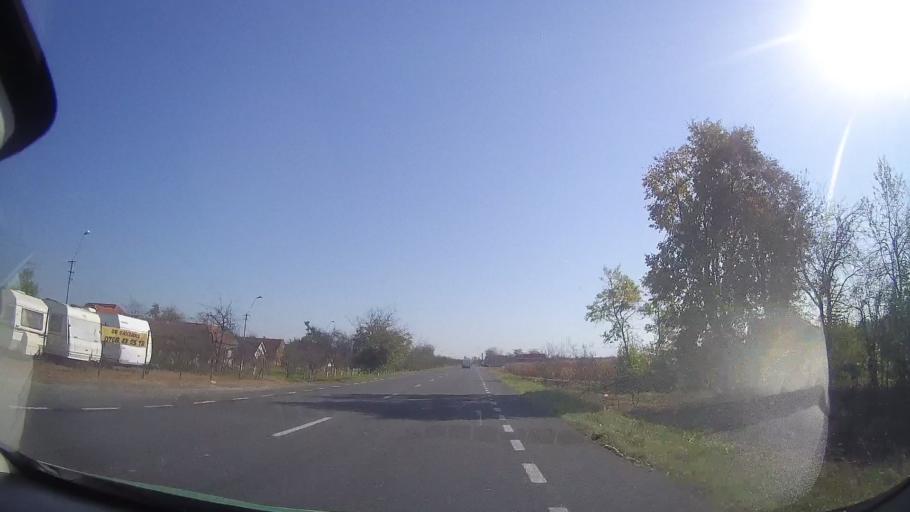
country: RO
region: Timis
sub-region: Comuna Belint
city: Belint
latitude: 45.7541
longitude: 21.7477
